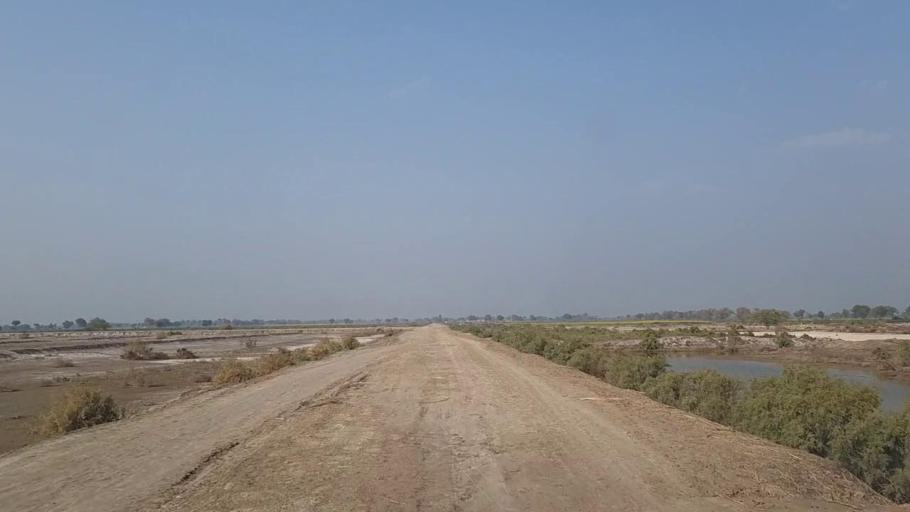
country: PK
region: Sindh
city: Nawabshah
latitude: 26.3414
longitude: 68.4739
